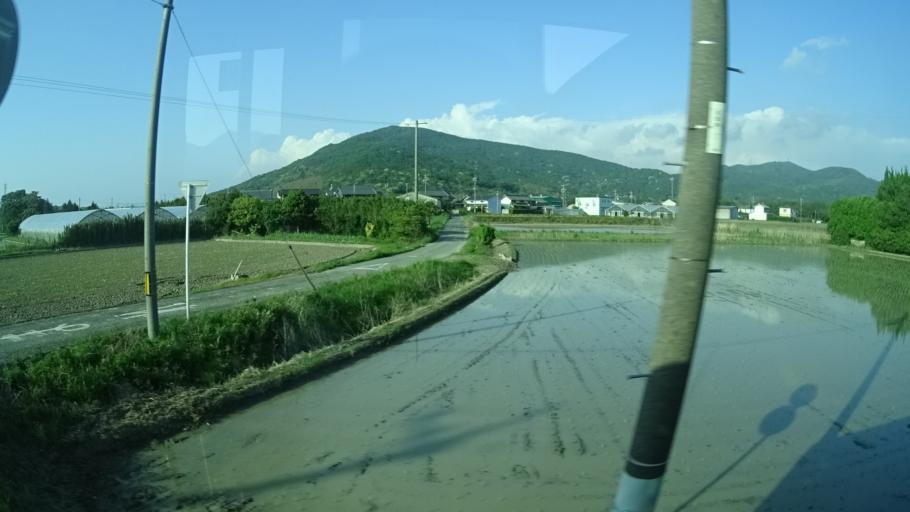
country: JP
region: Aichi
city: Tahara
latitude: 34.6575
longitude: 137.1996
